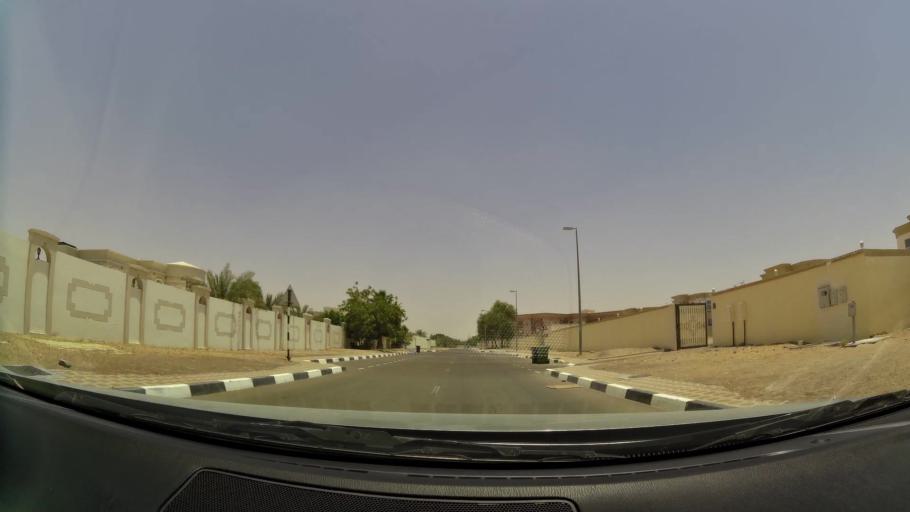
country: OM
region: Al Buraimi
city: Al Buraymi
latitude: 24.2848
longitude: 55.7404
